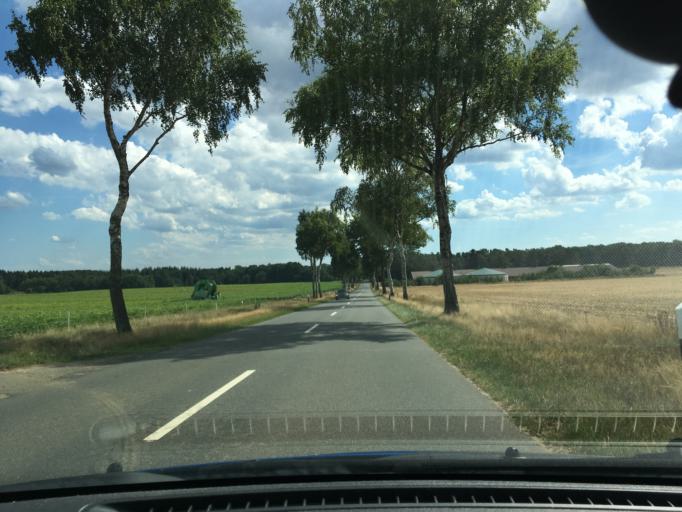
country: DE
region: Lower Saxony
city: Rehlingen
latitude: 53.0706
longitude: 10.2327
